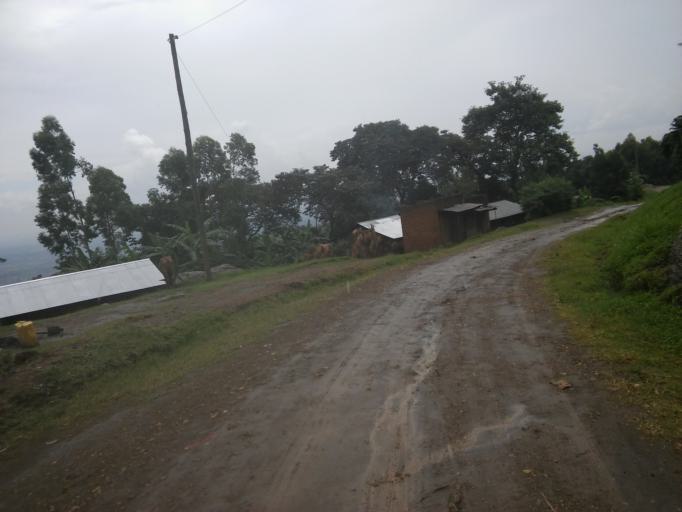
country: UG
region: Eastern Region
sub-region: Mbale District
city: Mbale
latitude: 1.0110
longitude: 34.2314
